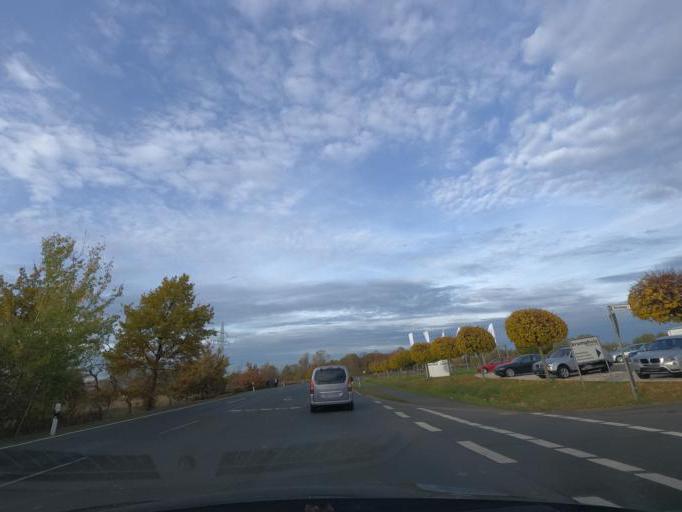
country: DE
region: Lower Saxony
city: Cremlingen
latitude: 52.2941
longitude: 10.5974
